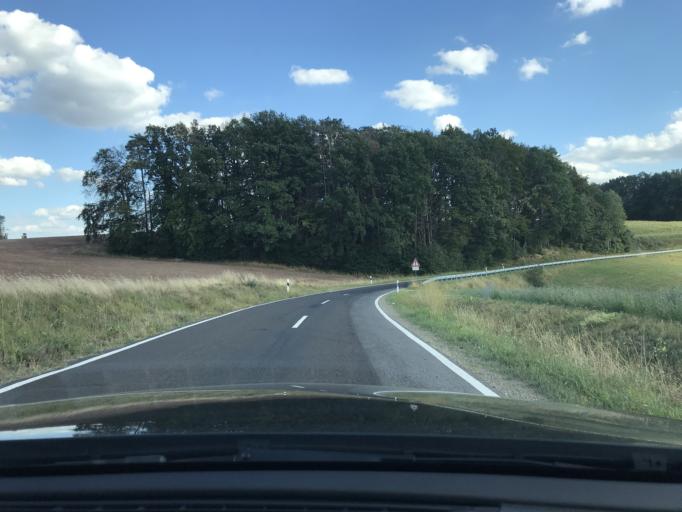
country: DE
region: Bavaria
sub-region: Regierungsbezirk Unterfranken
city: Kirchlauter
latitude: 50.0755
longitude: 10.6627
